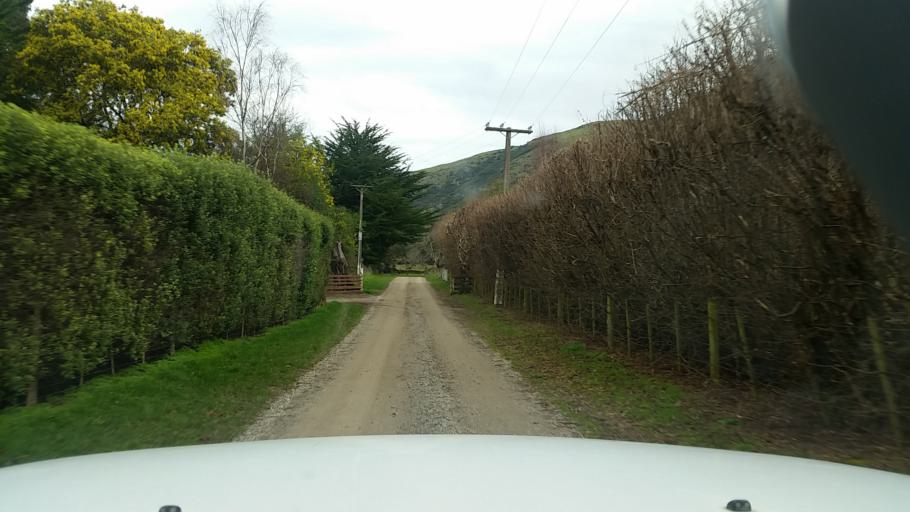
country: NZ
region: Canterbury
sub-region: Christchurch City
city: Christchurch
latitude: -43.7633
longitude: 172.7220
